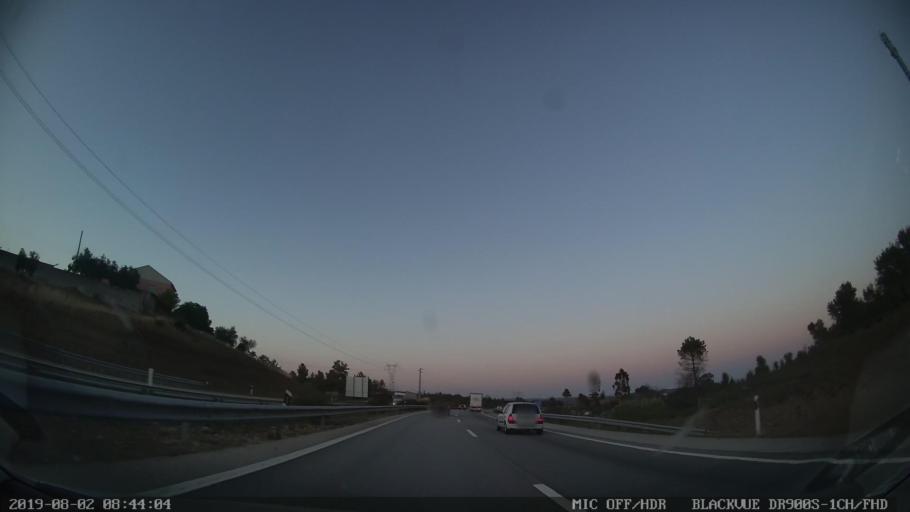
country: PT
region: Santarem
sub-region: Abrantes
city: Abrantes
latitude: 39.4916
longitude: -8.2066
